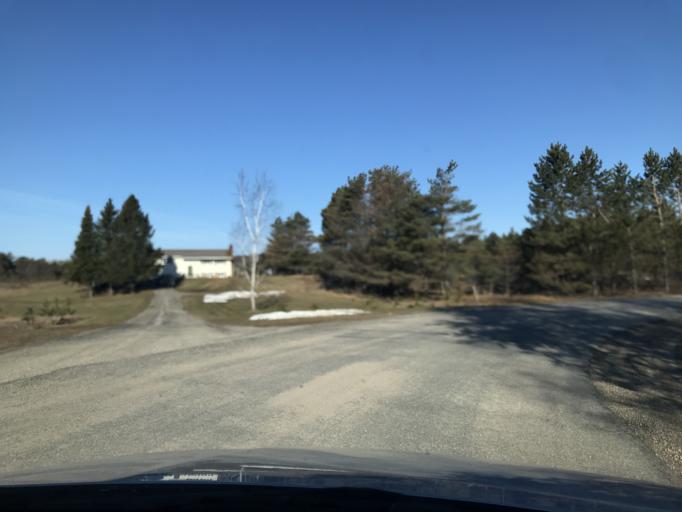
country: US
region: Wisconsin
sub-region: Marinette County
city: Peshtigo
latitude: 45.3561
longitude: -88.0292
